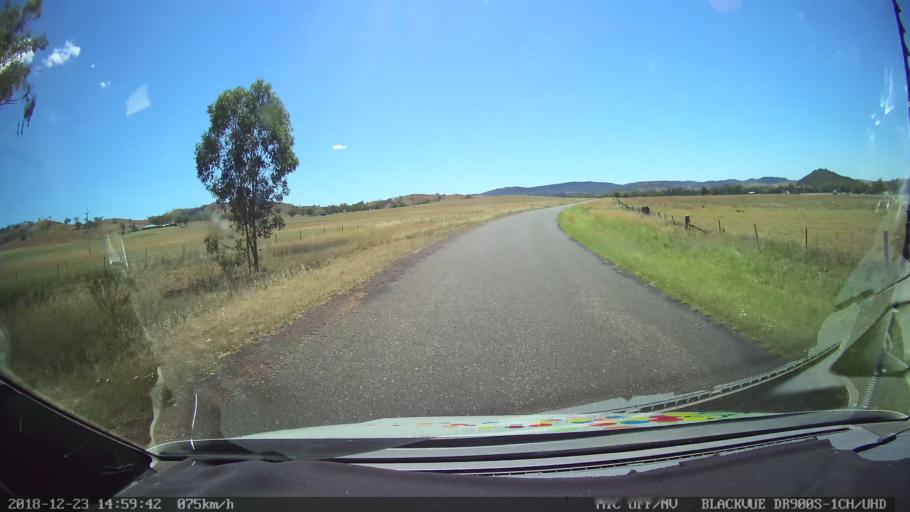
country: AU
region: New South Wales
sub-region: Tamworth Municipality
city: Manilla
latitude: -30.7249
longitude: 150.7974
